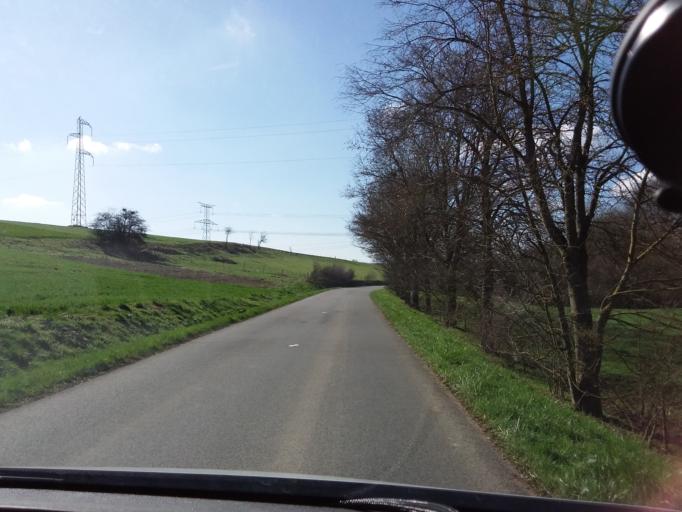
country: FR
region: Picardie
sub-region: Departement de l'Aisne
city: Hirson
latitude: 49.8864
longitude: 4.0975
